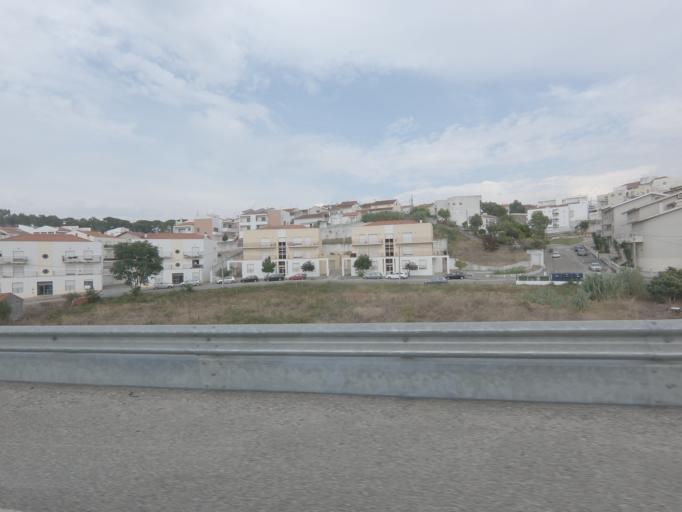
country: PT
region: Coimbra
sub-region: Coimbra
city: Coimbra
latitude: 40.1983
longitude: -8.4530
